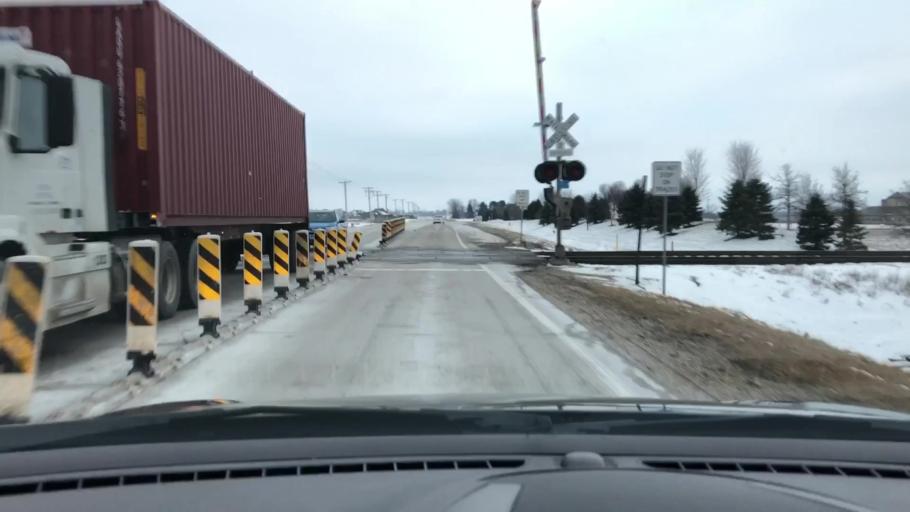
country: US
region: Illinois
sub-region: Will County
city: New Lenox
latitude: 41.4919
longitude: -88.0037
